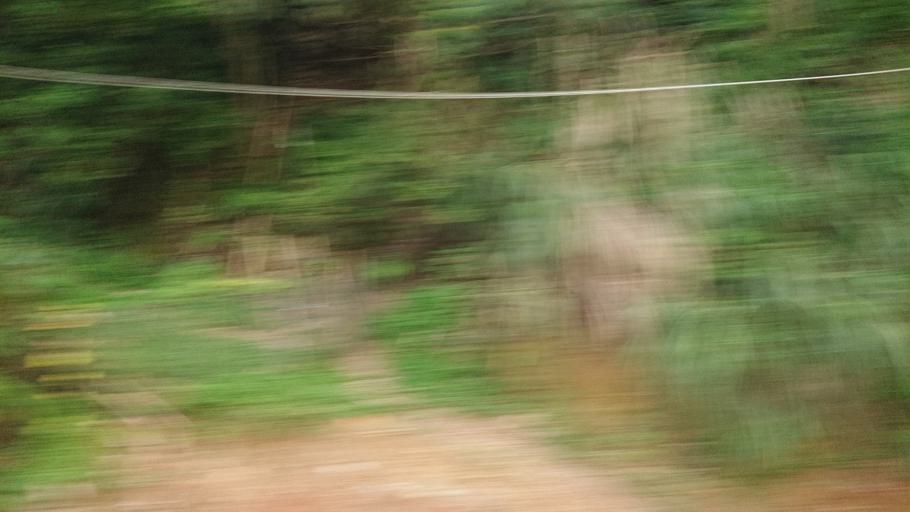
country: TW
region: Taiwan
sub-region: Nantou
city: Puli
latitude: 23.9757
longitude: 120.9893
